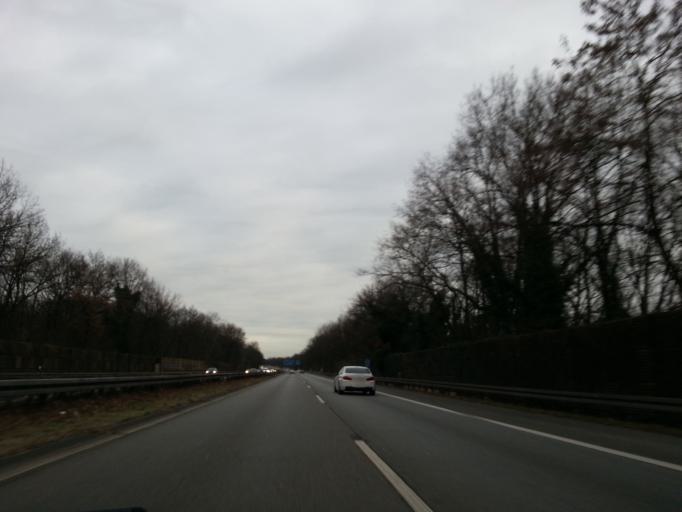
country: DE
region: North Rhine-Westphalia
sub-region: Regierungsbezirk Dusseldorf
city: Dinslaken
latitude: 51.5446
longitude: 6.8240
